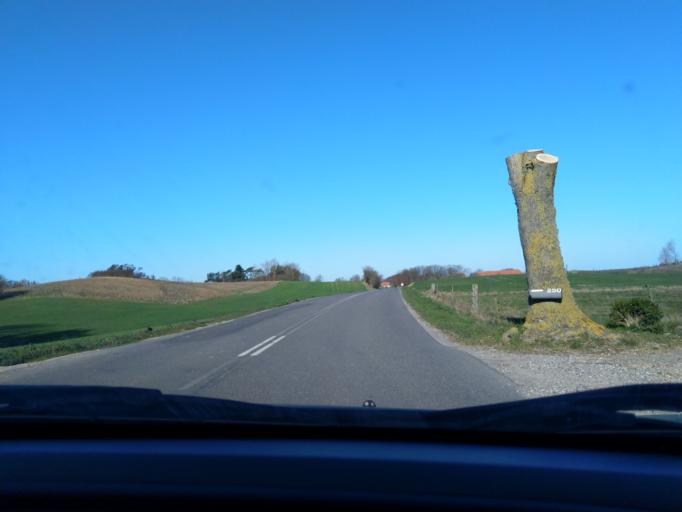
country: DK
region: Zealand
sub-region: Kalundborg Kommune
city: Kalundborg
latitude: 55.7302
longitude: 10.9864
